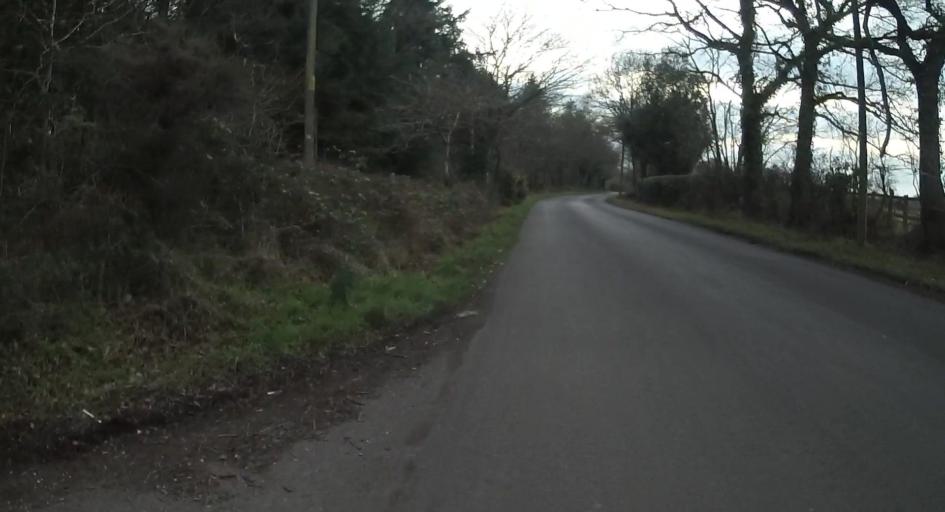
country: GB
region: England
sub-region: West Berkshire
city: Theale
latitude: 51.4056
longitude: -1.0743
